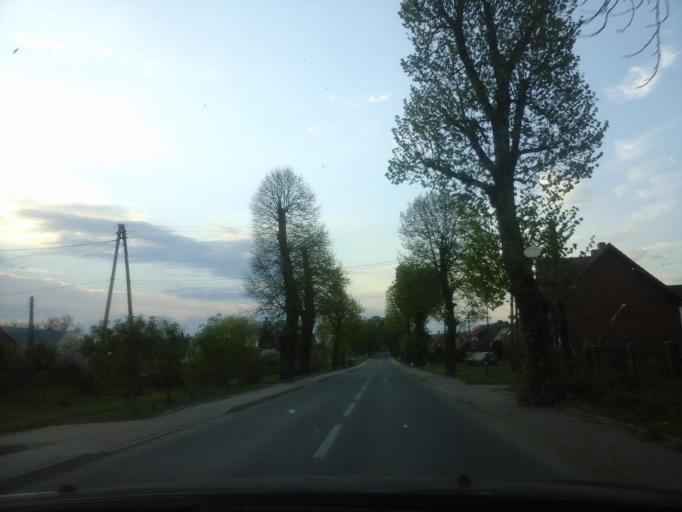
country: PL
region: West Pomeranian Voivodeship
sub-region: Powiat choszczenski
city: Pelczyce
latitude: 53.0185
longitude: 15.3699
